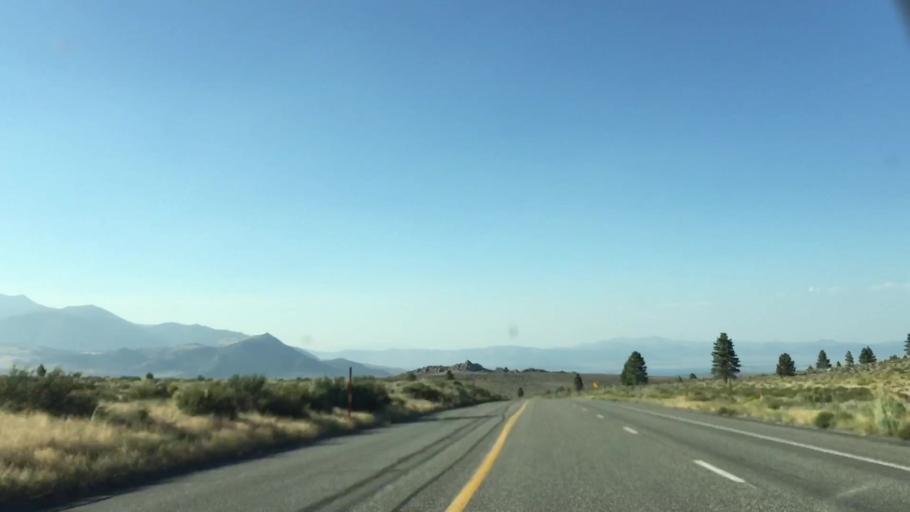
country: US
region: California
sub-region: Mono County
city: Mammoth Lakes
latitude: 37.8353
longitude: -119.0697
